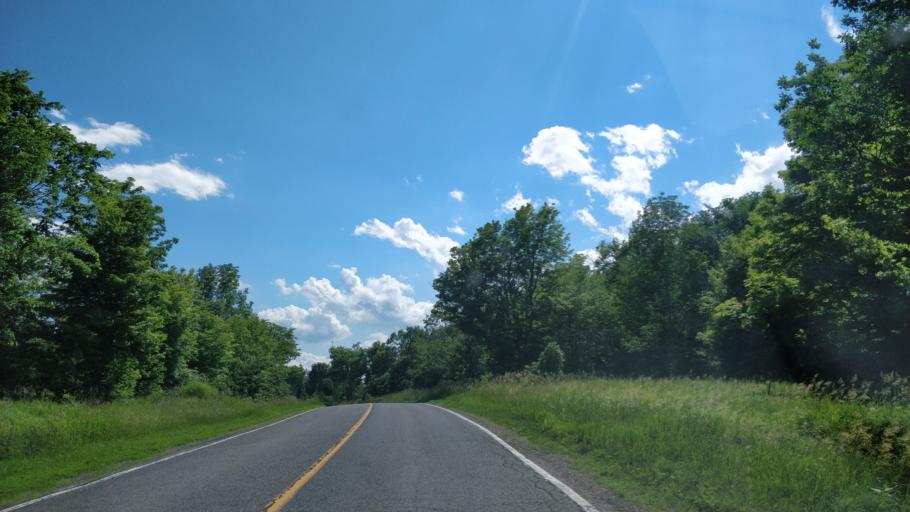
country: CA
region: Ontario
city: Perth
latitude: 44.7558
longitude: -76.4815
